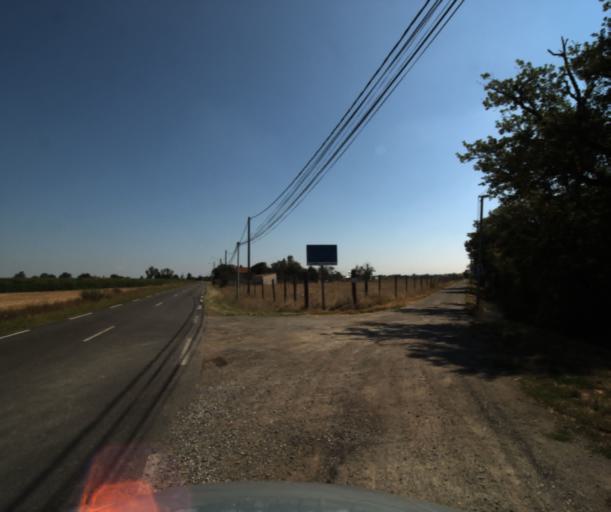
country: FR
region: Midi-Pyrenees
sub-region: Departement de la Haute-Garonne
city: Labastidette
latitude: 43.4691
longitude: 1.2530
